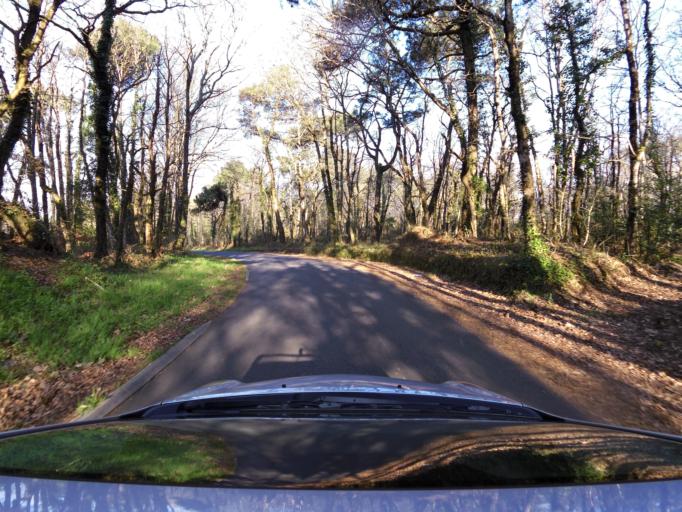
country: FR
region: Brittany
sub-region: Departement du Morbihan
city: Guidel-Plage
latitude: 47.7802
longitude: -3.4936
